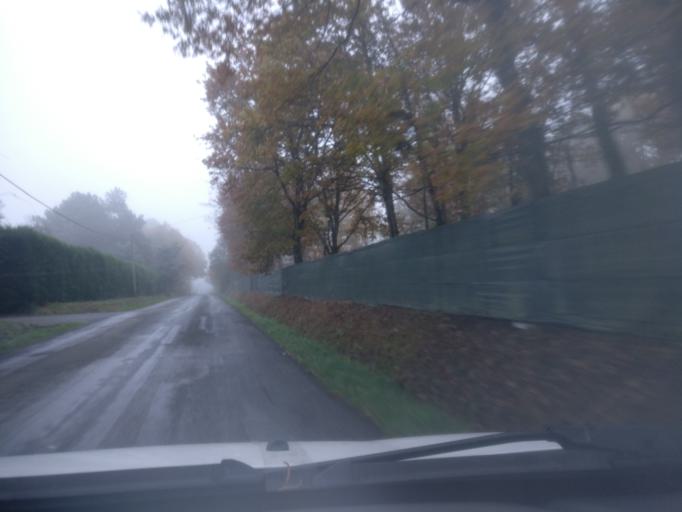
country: FR
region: Brittany
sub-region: Departement d'Ille-et-Vilaine
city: Laille
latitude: 47.9926
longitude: -1.7206
